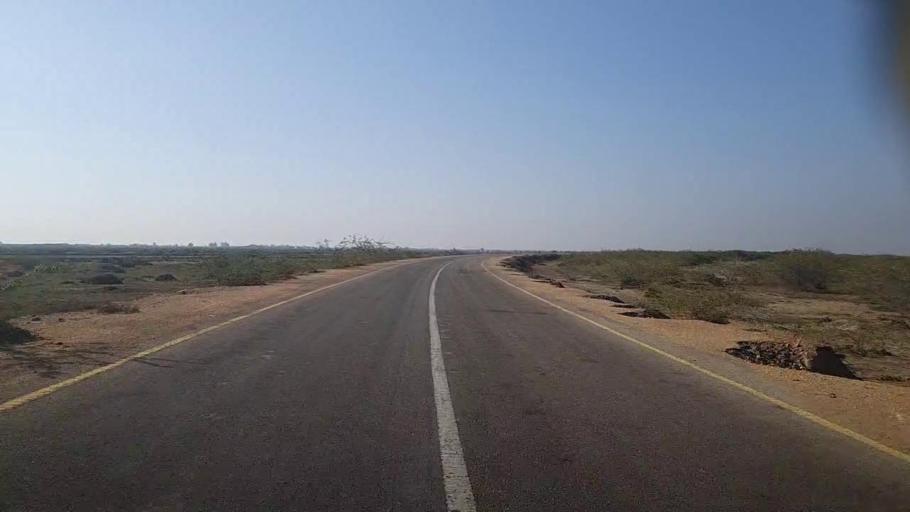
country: PK
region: Sindh
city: Mirpur Sakro
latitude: 24.5614
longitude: 67.4992
